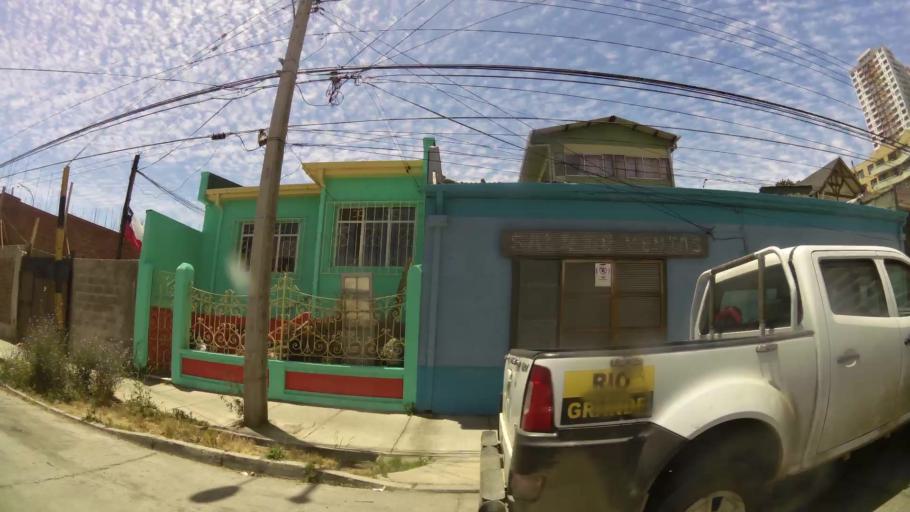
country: CL
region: Valparaiso
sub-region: Provincia de Valparaiso
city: Valparaiso
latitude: -33.0391
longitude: -71.5940
